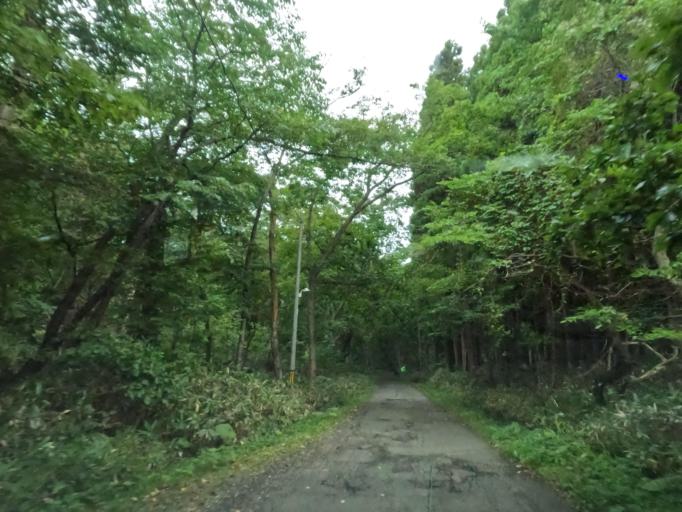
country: JP
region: Hokkaido
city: Muroran
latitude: 42.3685
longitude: 140.9746
